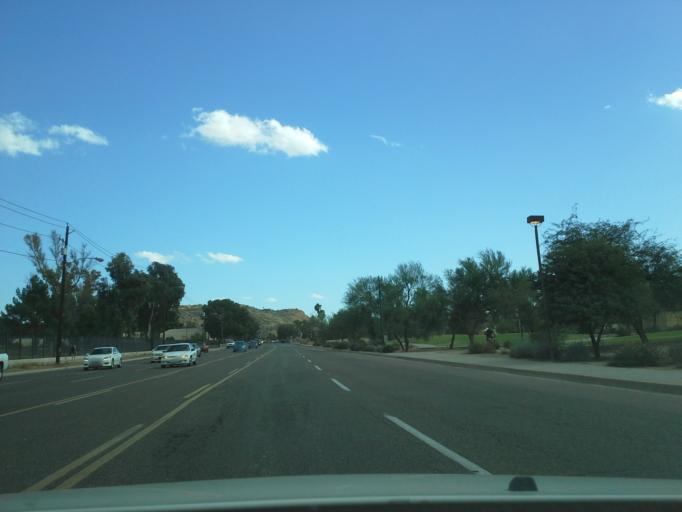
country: US
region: Arizona
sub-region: Maricopa County
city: Glendale
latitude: 33.6109
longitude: -112.1100
